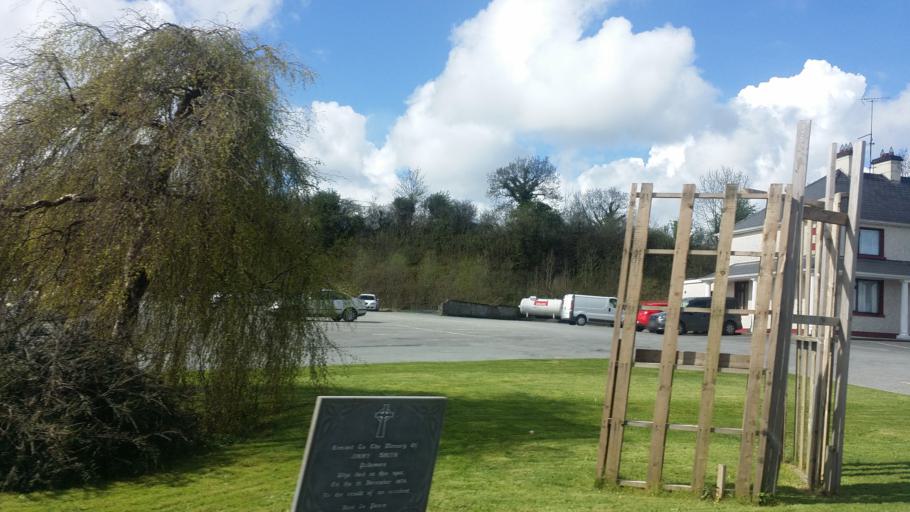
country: IE
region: Ulster
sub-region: An Cabhan
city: Cavan
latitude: 53.9838
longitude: -7.3454
